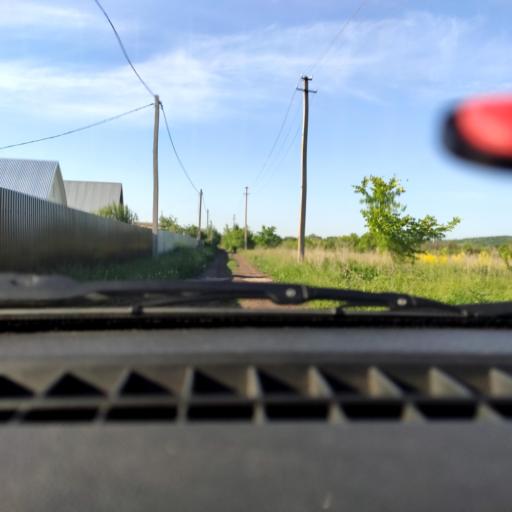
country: RU
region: Bashkortostan
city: Avdon
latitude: 54.4623
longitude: 55.8191
